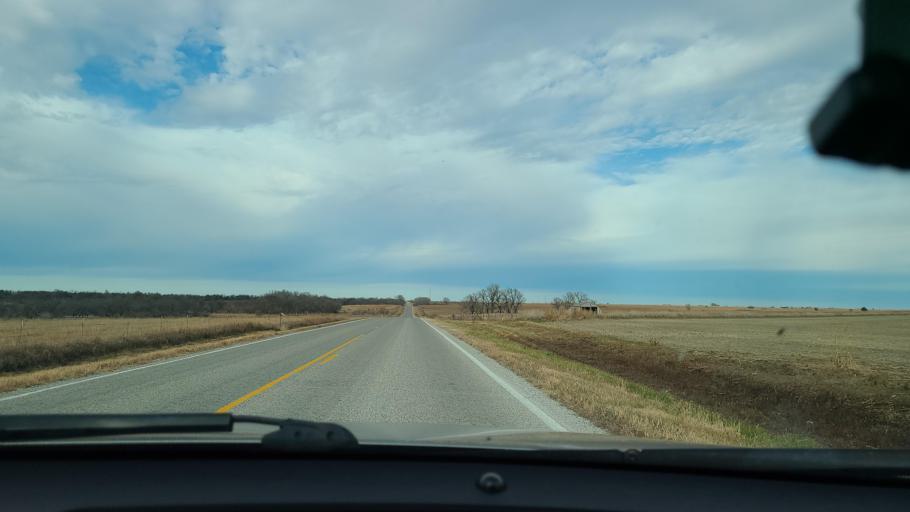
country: US
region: Kansas
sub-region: McPherson County
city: Inman
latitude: 38.3346
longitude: -97.9245
